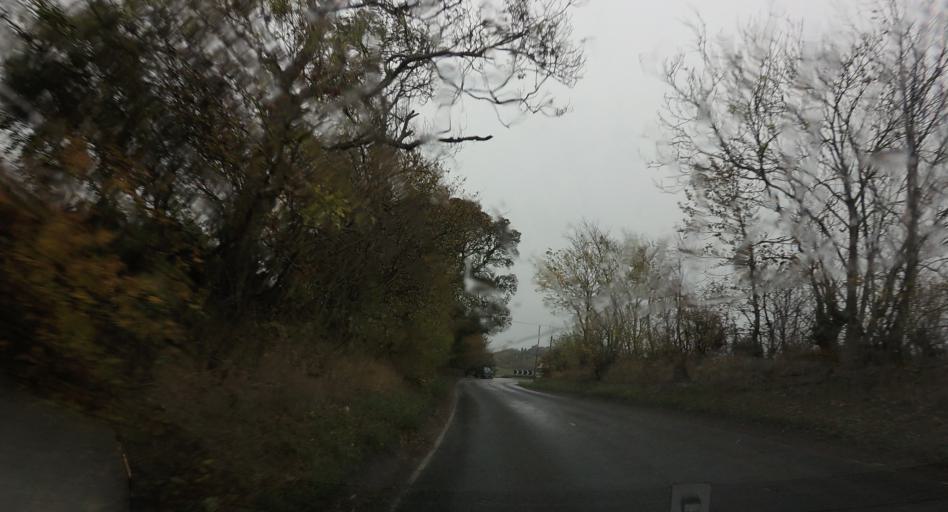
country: GB
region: Scotland
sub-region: Perth and Kinross
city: Coupar Angus
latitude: 56.5533
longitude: -3.2866
